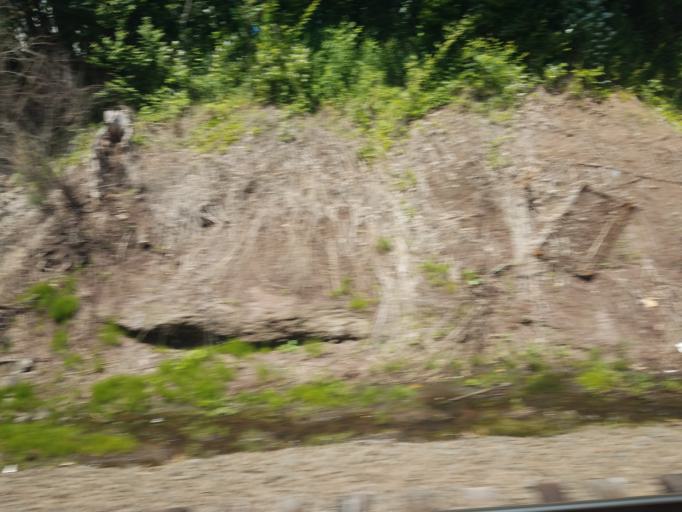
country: US
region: Connecticut
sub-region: New Haven County
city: Meriden
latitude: 41.5202
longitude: -72.8115
